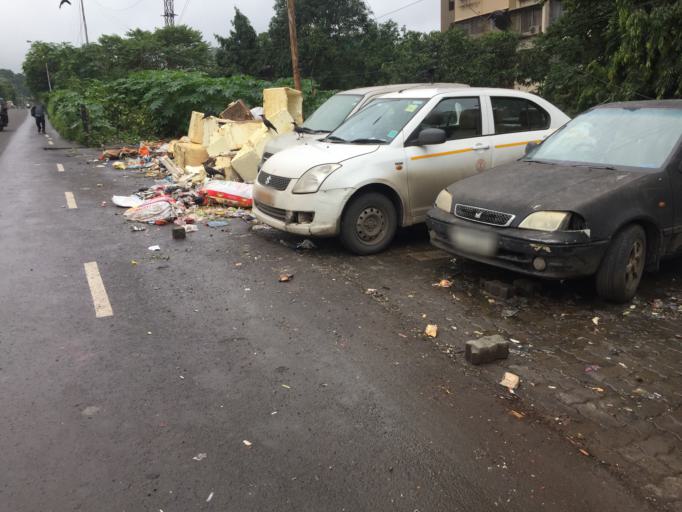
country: IN
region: Maharashtra
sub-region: Thane
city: Thane
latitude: 19.1650
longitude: 72.9352
